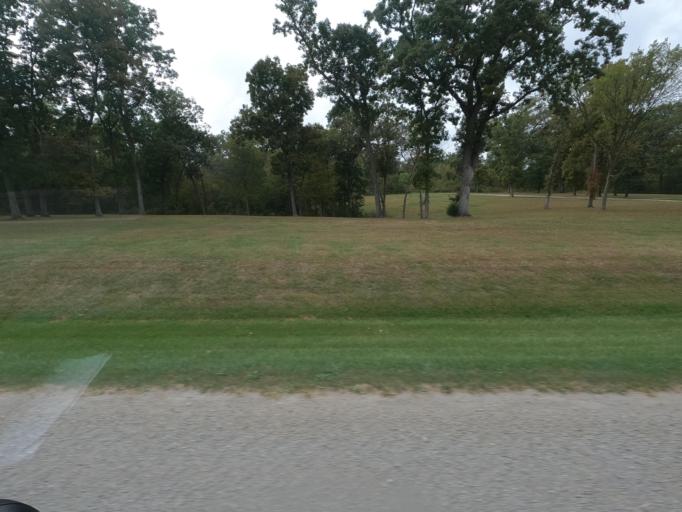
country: US
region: Iowa
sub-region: Wapello County
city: Ottumwa
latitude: 40.9406
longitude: -92.2270
